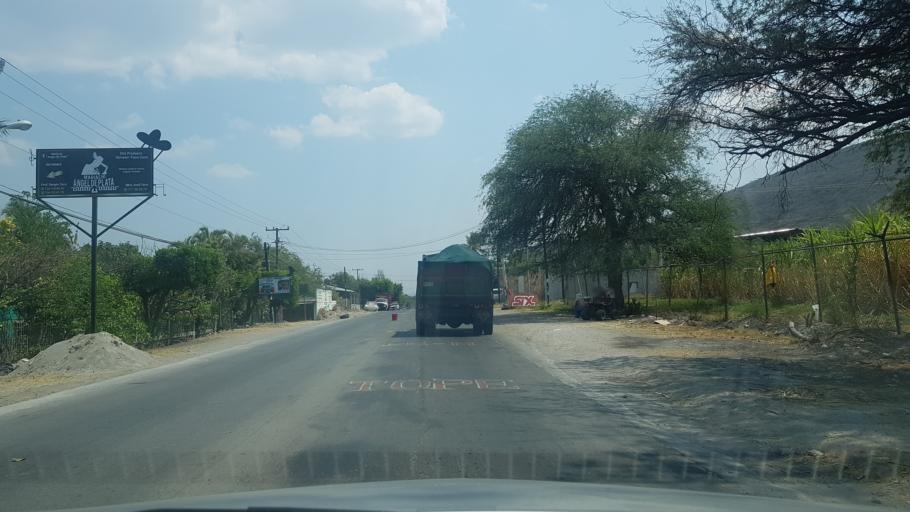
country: MX
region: Morelos
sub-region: Tlaltizapan de Zapata
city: Colonia Palo Prieto (Chipitongo)
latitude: 18.7210
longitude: -99.1211
